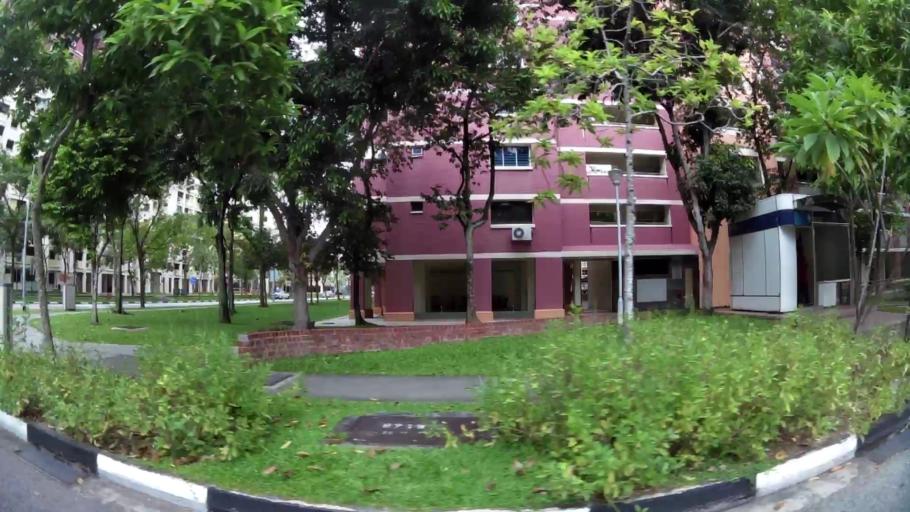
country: SG
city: Singapore
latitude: 1.3586
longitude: 103.9350
